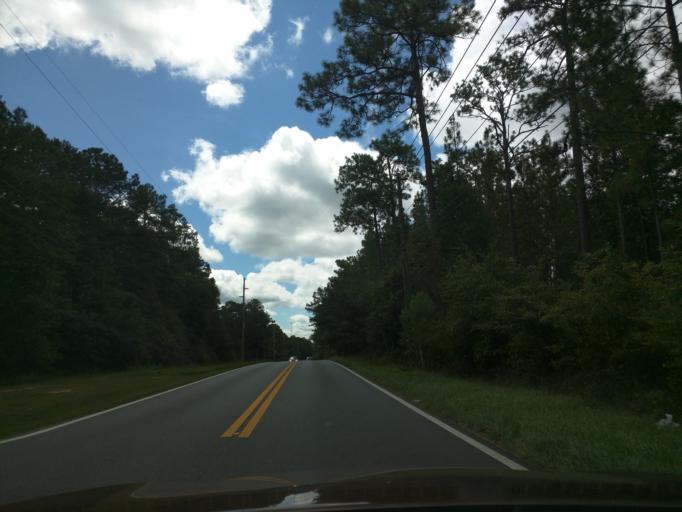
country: US
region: Florida
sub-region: Leon County
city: Tallahassee
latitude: 30.5738
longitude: -84.2299
